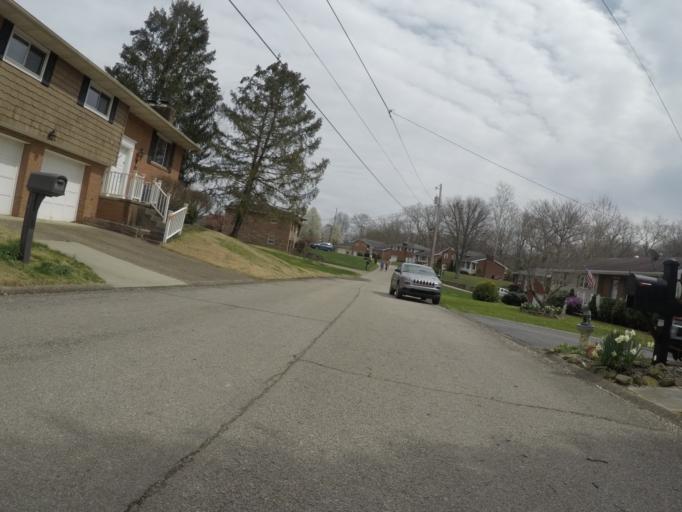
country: US
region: West Virginia
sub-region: Cabell County
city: Pea Ridge
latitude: 38.4224
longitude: -82.3244
